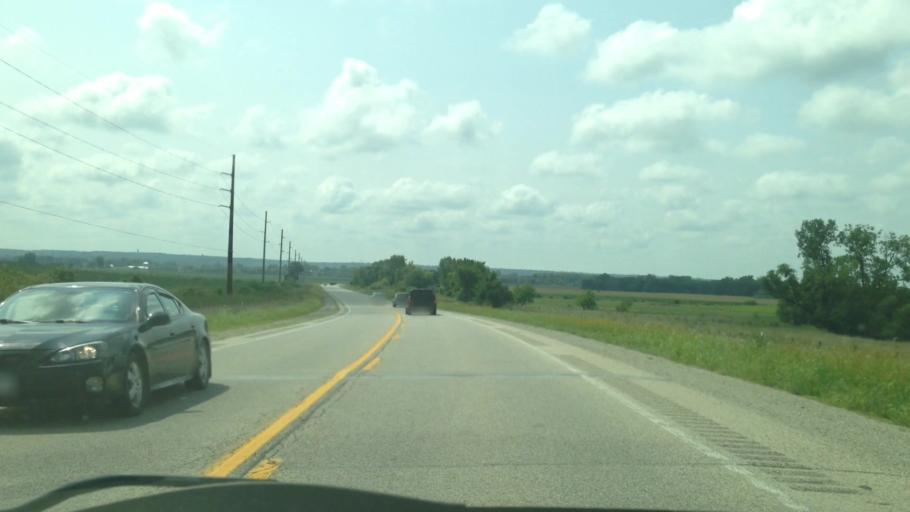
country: US
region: Iowa
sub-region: Benton County
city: Walford
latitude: 41.8220
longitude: -91.8731
